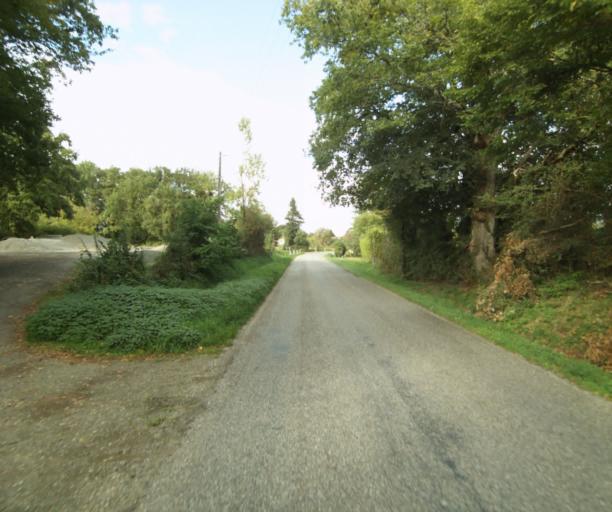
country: FR
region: Midi-Pyrenees
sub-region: Departement du Gers
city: Eauze
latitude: 43.8737
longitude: 0.1003
